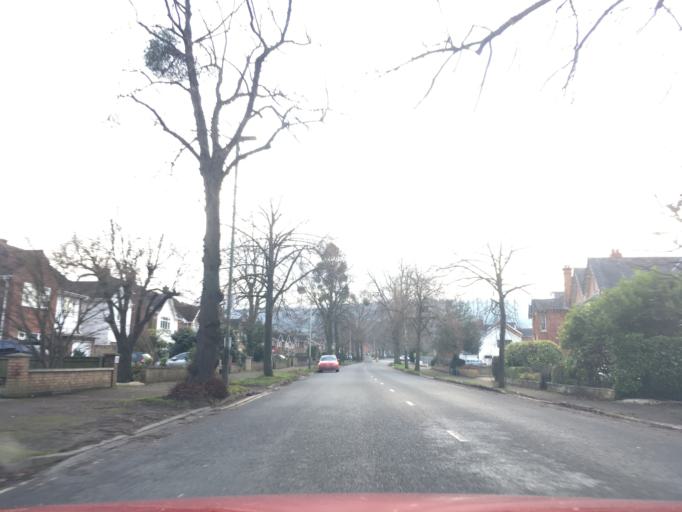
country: GB
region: England
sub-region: Gloucestershire
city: Cheltenham
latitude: 51.8820
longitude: -2.0786
